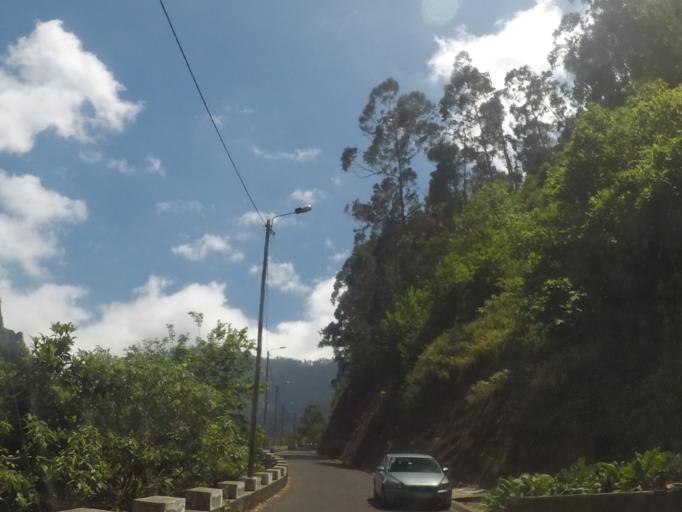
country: PT
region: Madeira
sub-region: Camara de Lobos
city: Curral das Freiras
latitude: 32.7182
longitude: -16.9696
